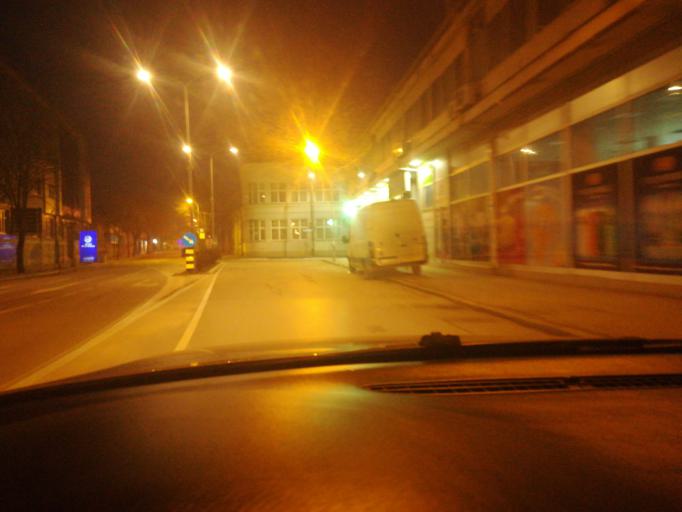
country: RS
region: Central Serbia
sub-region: Branicevski Okrug
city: Pozarevac
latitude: 44.6194
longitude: 21.1835
